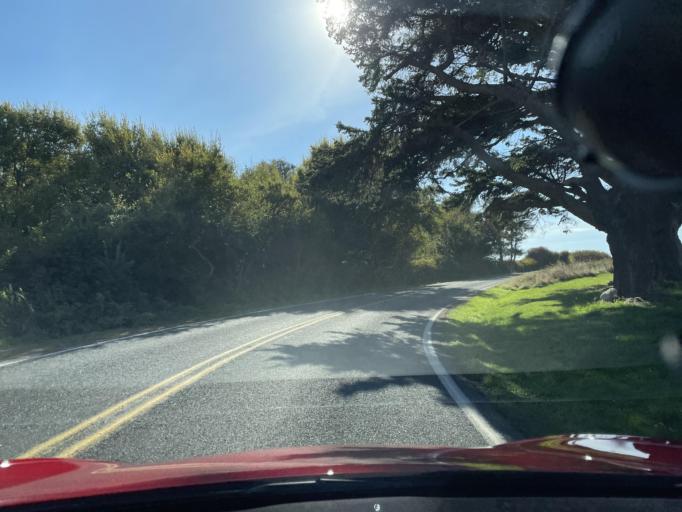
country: US
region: Washington
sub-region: San Juan County
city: Friday Harbor
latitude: 48.4540
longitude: -122.9633
